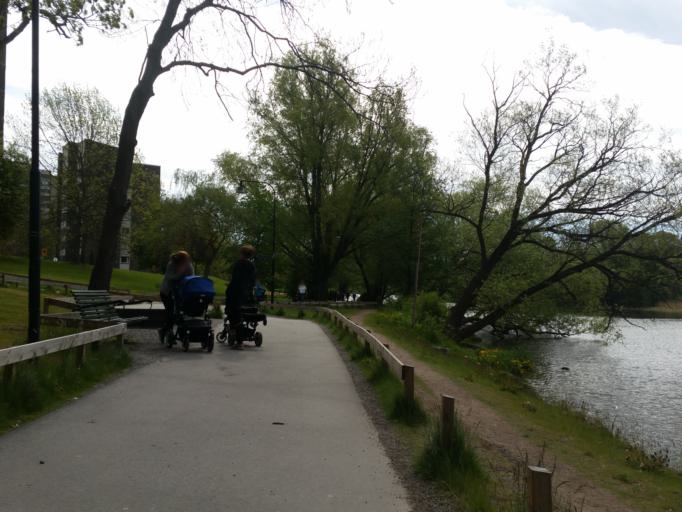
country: SE
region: Stockholm
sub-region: Stockholms Kommun
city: Arsta
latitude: 59.3100
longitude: 18.0447
